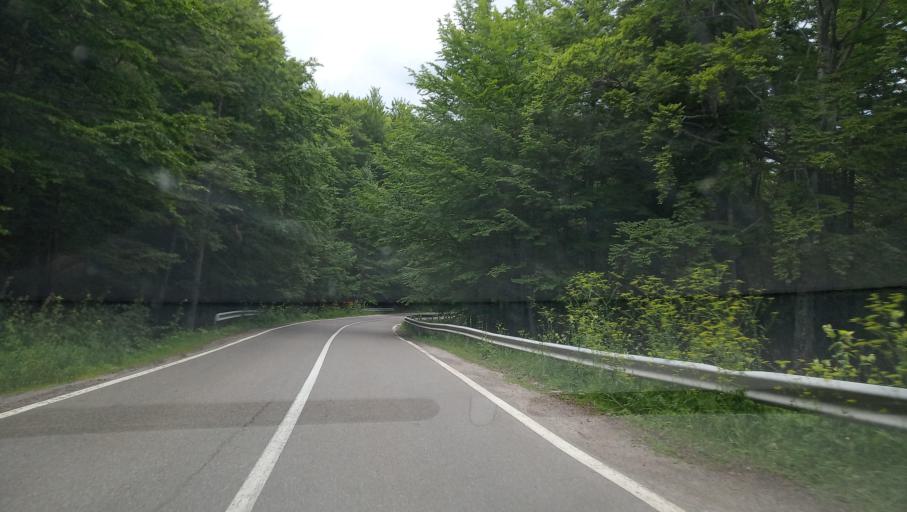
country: RO
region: Prahova
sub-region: Oras Sinaia
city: Sinaia
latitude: 45.3113
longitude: 25.5215
